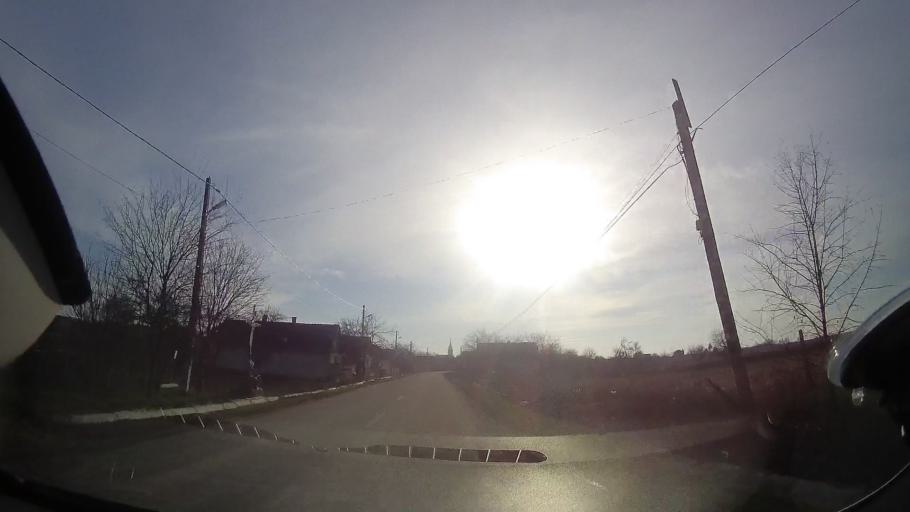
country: RO
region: Bihor
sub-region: Comuna Sarbi
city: Sarbi
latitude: 47.2105
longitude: 22.1318
